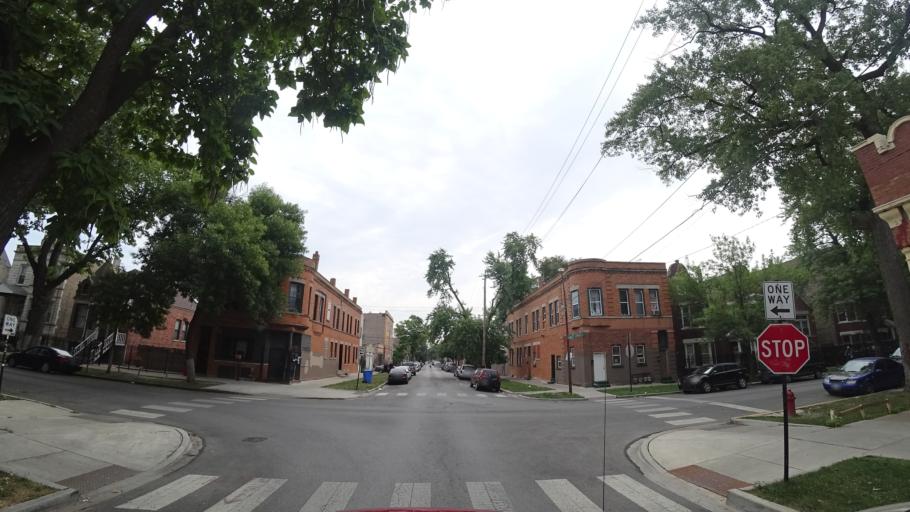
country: US
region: Illinois
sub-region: Cook County
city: Cicero
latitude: 41.8480
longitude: -87.7127
